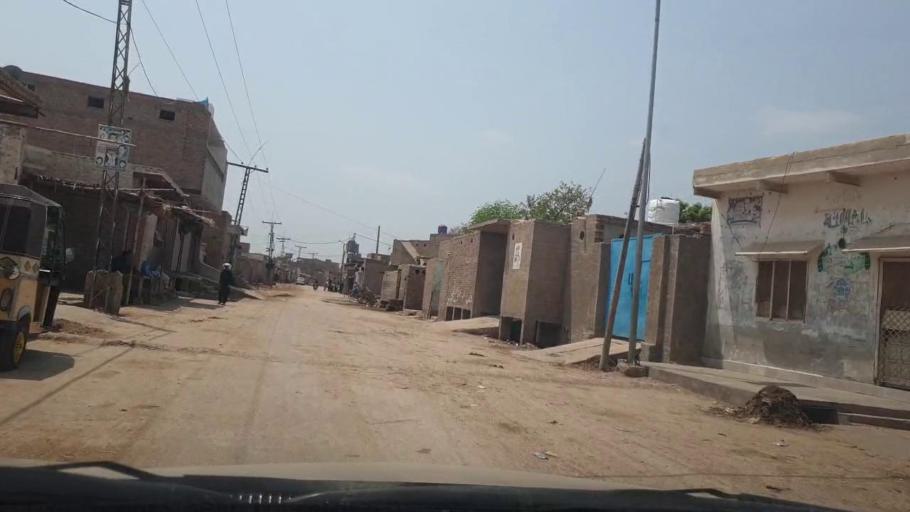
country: PK
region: Sindh
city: Ratodero
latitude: 27.7259
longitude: 68.2821
